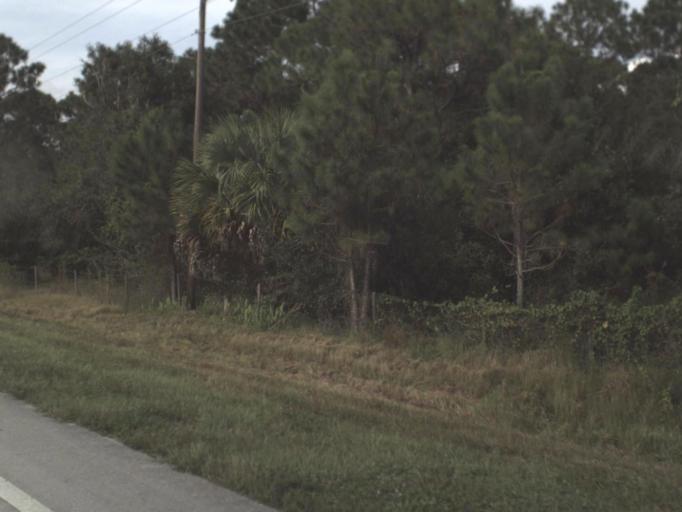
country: US
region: Florida
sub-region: Okeechobee County
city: Taylor Creek
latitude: 27.2187
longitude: -80.7629
